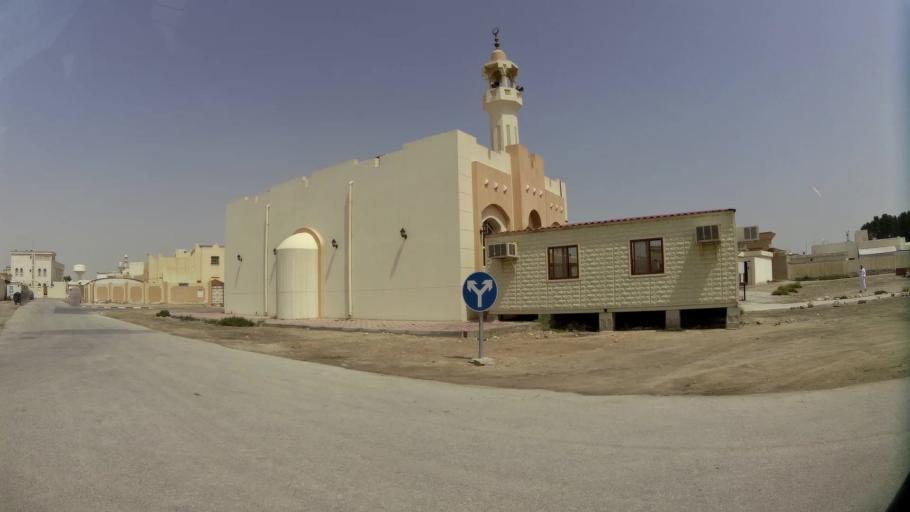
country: QA
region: Baladiyat ar Rayyan
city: Ar Rayyan
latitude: 25.2366
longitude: 51.4183
